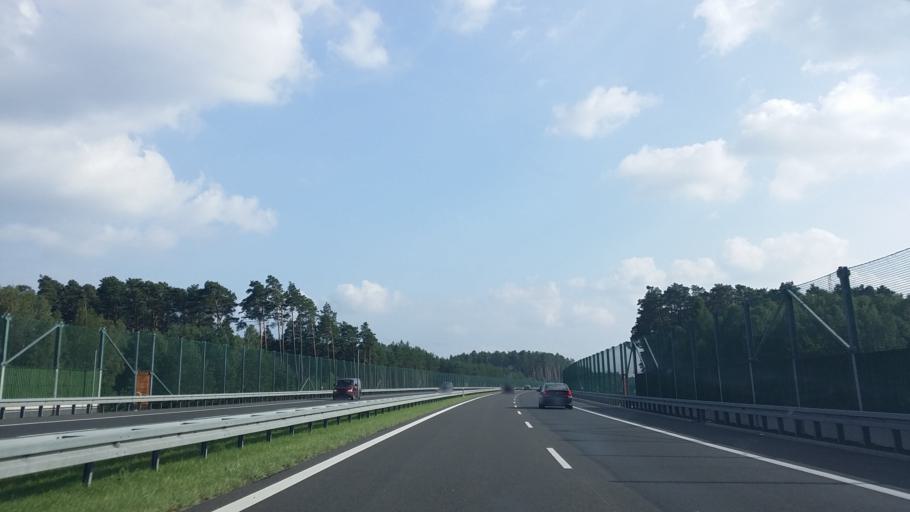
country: PL
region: Lubusz
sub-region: Powiat miedzyrzecki
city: Miedzyrzecz
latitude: 52.5020
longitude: 15.5544
